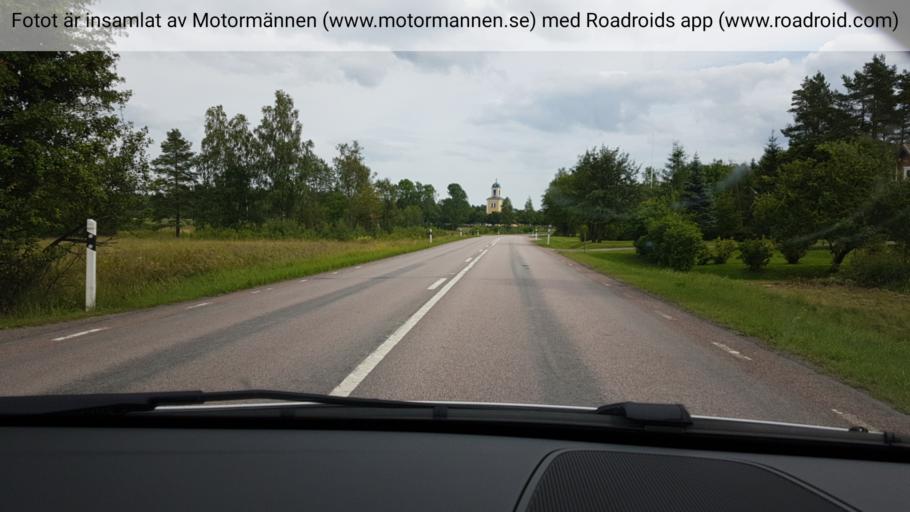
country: SE
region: Uppsala
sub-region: Osthammars Kommun
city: OEsthammar
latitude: 60.2423
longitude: 18.3348
